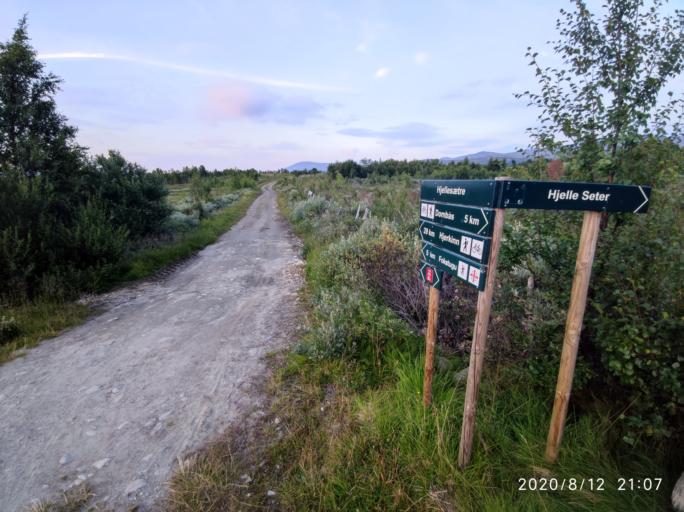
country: NO
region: Oppland
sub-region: Dovre
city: Dombas
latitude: 62.0915
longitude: 9.2068
